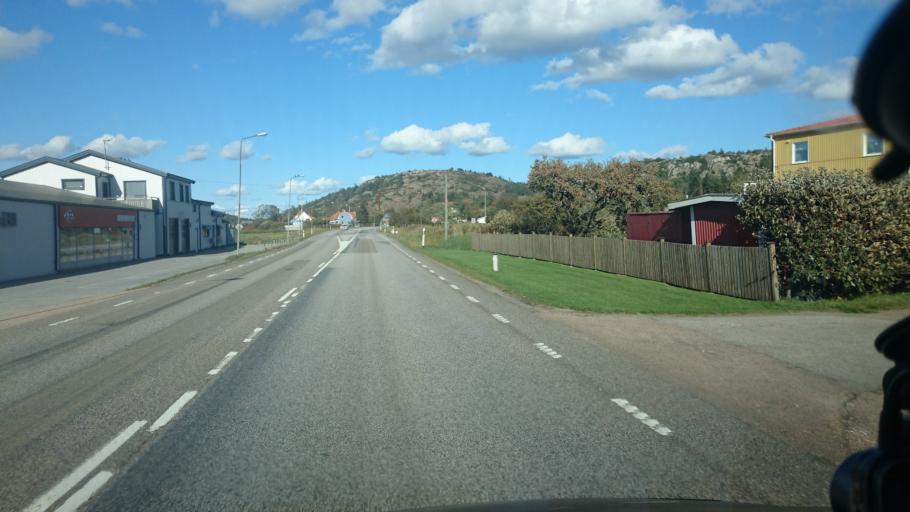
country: SE
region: Vaestra Goetaland
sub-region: Lysekils Kommun
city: Brastad
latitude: 58.3212
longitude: 11.4903
